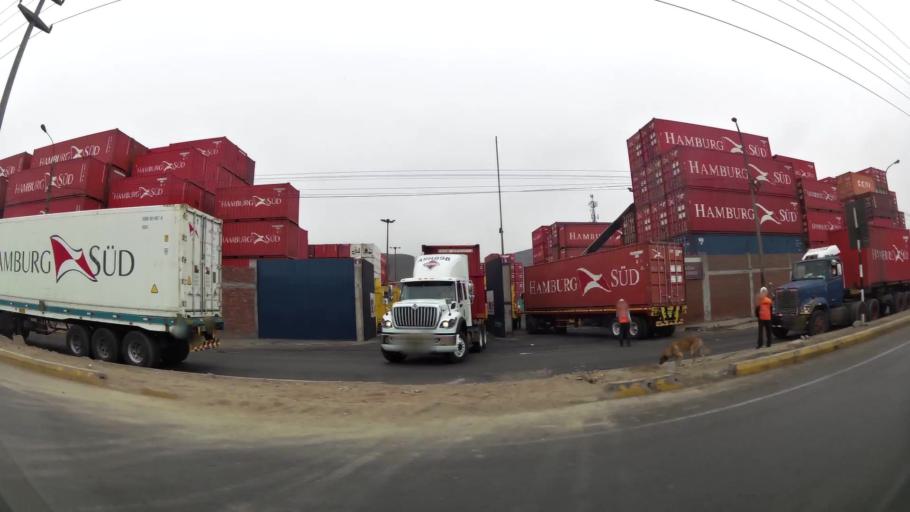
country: PE
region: Lima
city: Ventanilla
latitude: -11.9568
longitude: -77.1291
